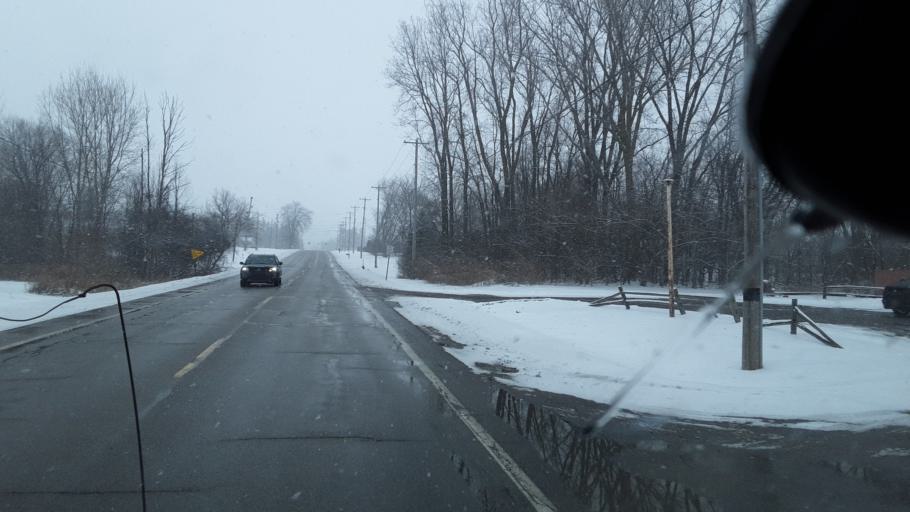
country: US
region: Michigan
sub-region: Jackson County
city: Jackson
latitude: 42.2876
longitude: -84.3995
